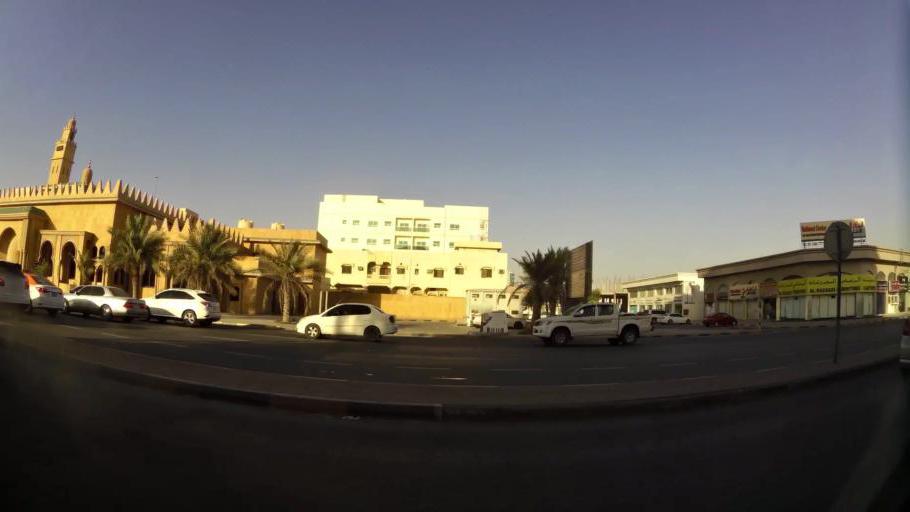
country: AE
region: Ajman
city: Ajman
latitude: 25.3976
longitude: 55.5047
